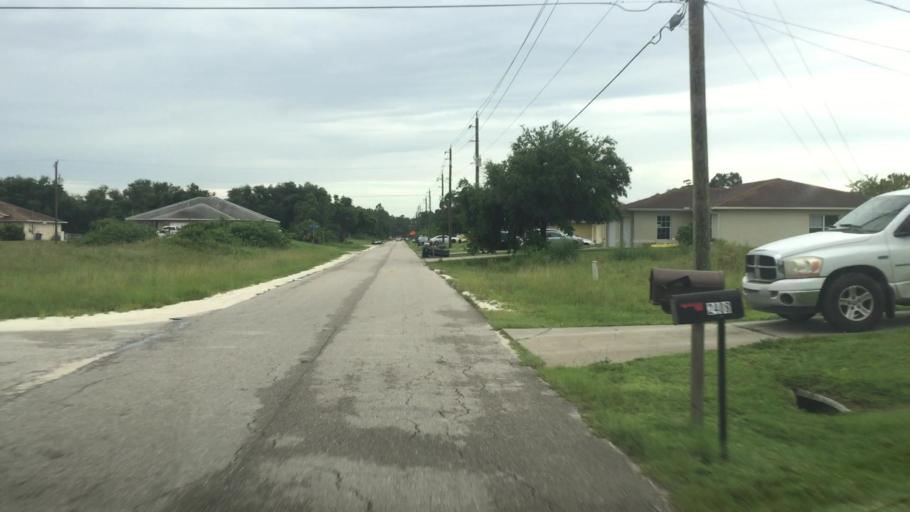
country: US
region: Florida
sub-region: Lee County
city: Gateway
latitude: 26.5918
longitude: -81.7214
